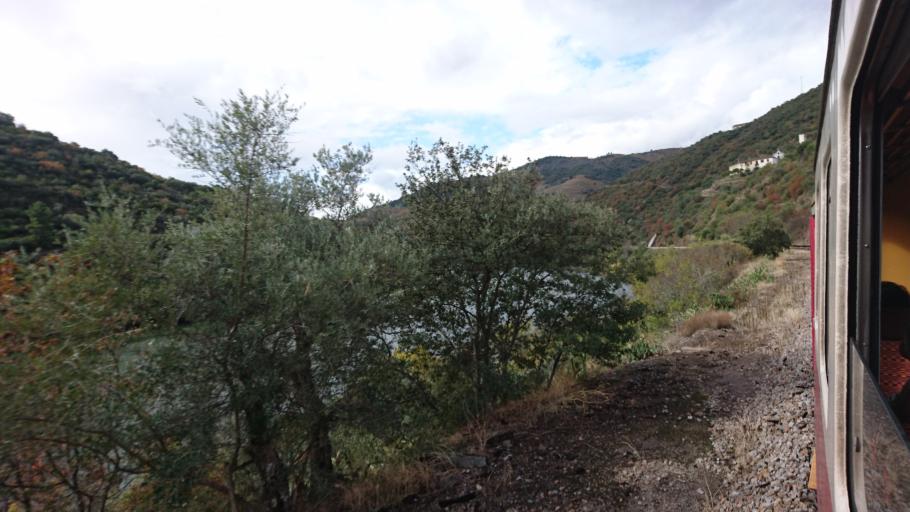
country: PT
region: Viseu
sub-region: Sao Joao da Pesqueira
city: Sao Joao da Pesqueira
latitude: 41.2004
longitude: -7.4948
